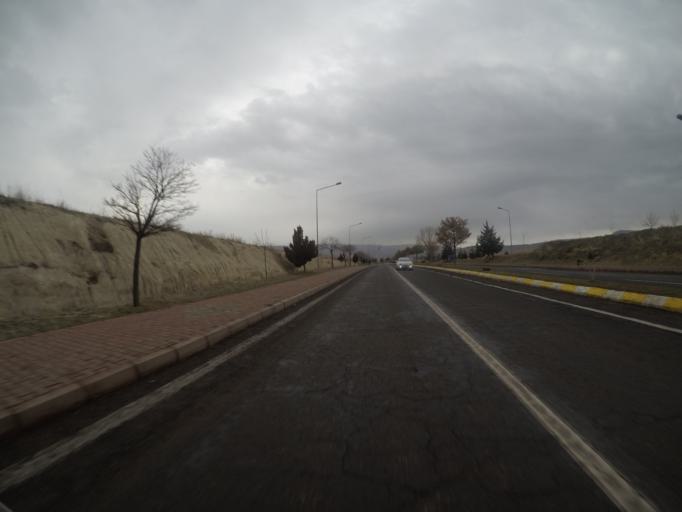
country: TR
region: Nevsehir
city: Urgub
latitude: 38.6338
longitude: 34.8960
